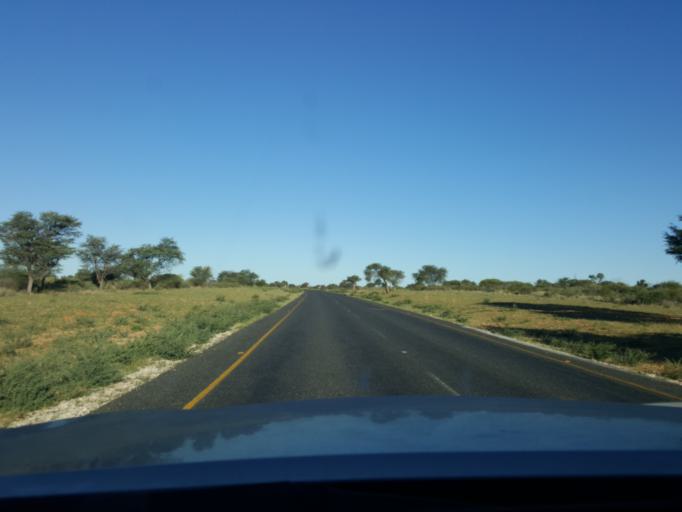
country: BW
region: Southern
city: Khakhea
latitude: -24.2252
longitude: 23.2382
